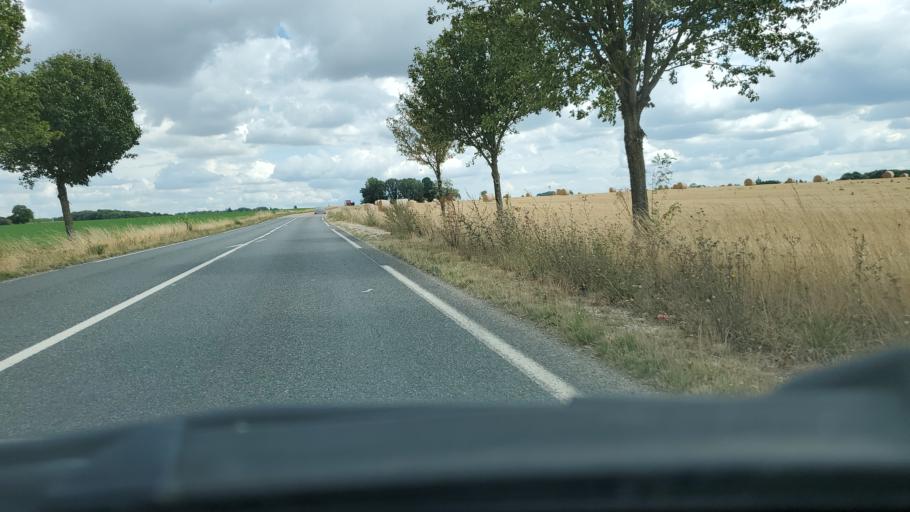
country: FR
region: Ile-de-France
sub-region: Departement de Seine-et-Marne
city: Fublaines
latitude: 48.9102
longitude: 2.9234
